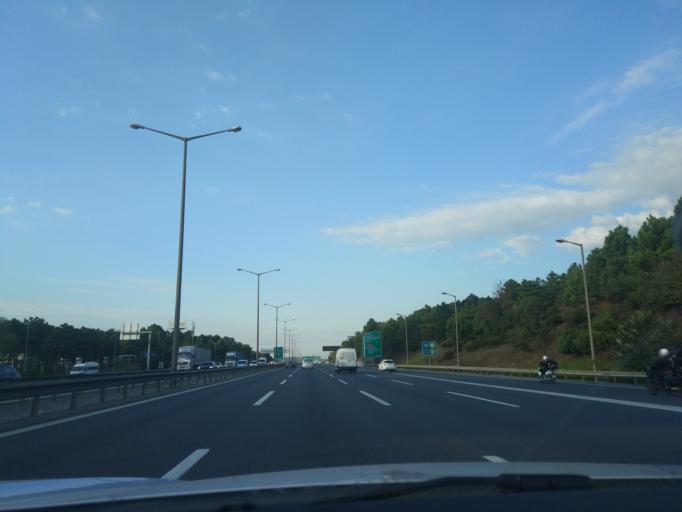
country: TR
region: Istanbul
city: Umraniye
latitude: 41.0350
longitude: 29.1212
